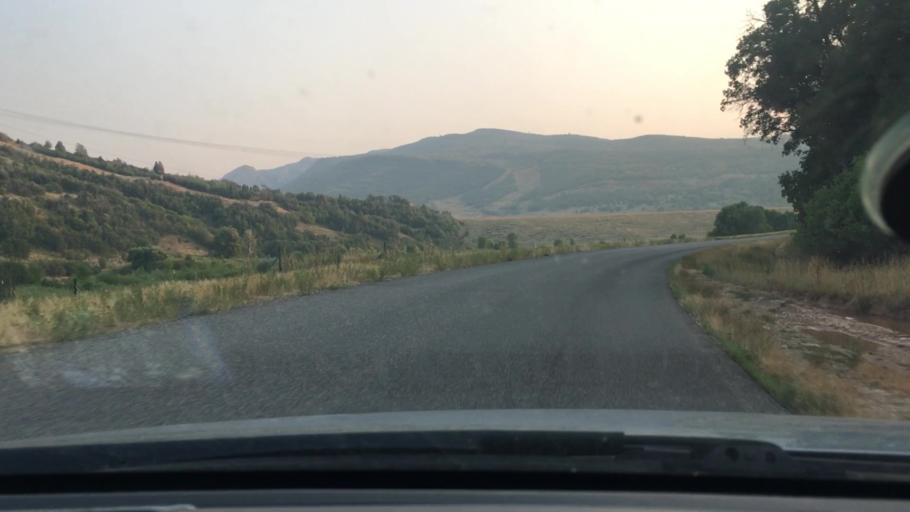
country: US
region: Utah
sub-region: Utah County
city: Mapleton
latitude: 40.0329
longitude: -111.4978
